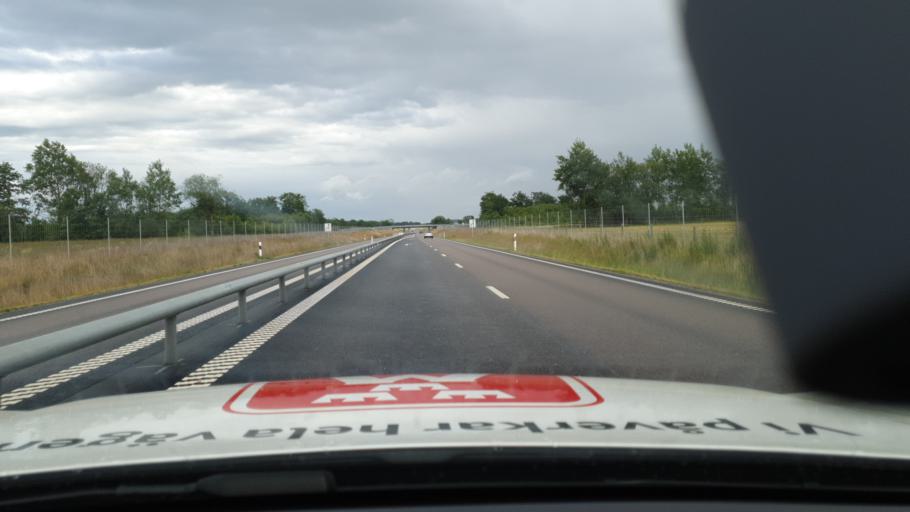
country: SE
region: Vaestra Goetaland
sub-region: Lidkopings Kommun
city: Vinninga
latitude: 58.4788
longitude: 13.2248
